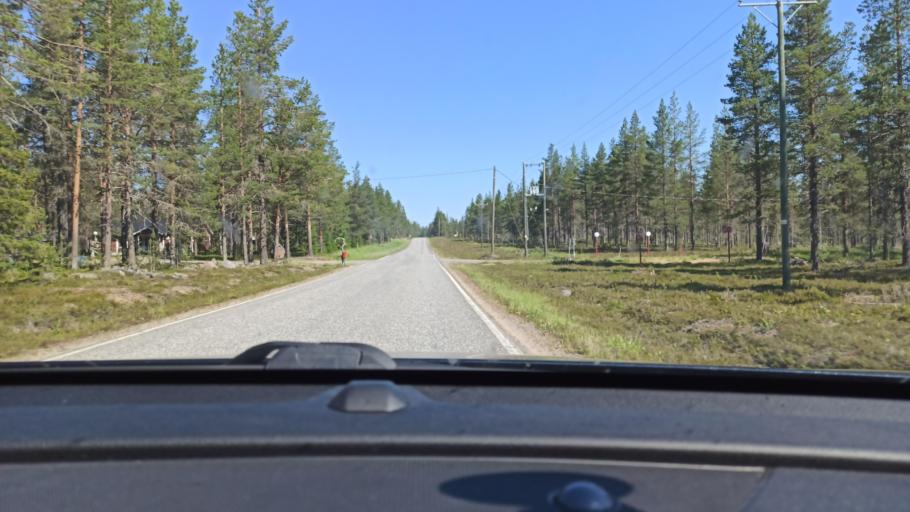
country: FI
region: Lapland
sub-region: Tunturi-Lappi
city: Kolari
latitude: 67.6519
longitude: 24.1626
